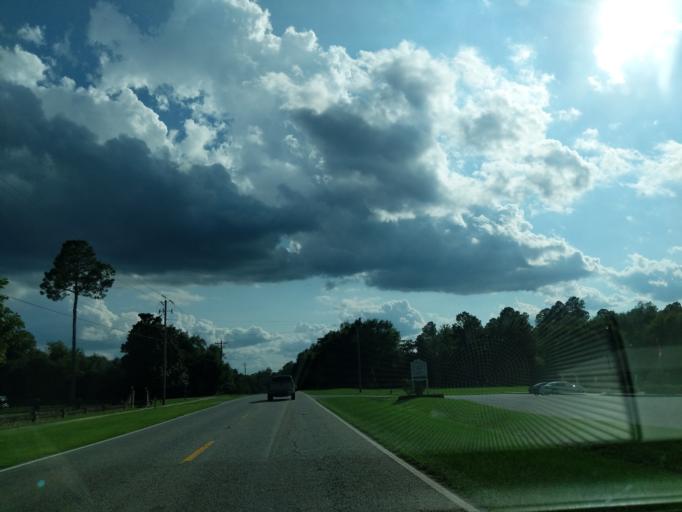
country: US
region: South Carolina
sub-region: Barnwell County
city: Williston
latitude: 33.4110
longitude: -81.4118
